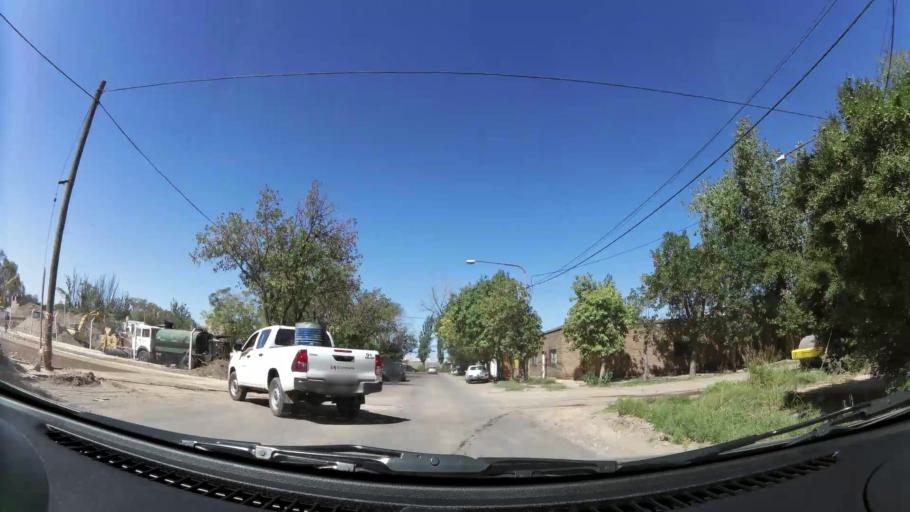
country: AR
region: Mendoza
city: Villa Nueva
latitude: -32.8936
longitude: -68.8019
